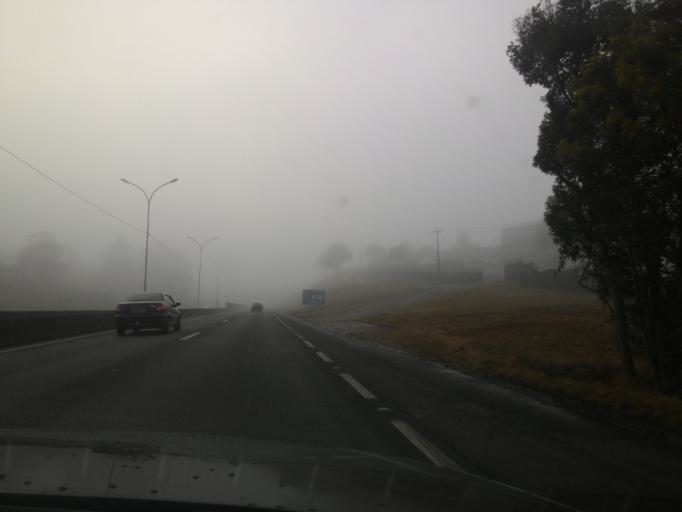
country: BR
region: Parana
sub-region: Quatro Barras
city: Quatro Barras
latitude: -25.3698
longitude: -49.1171
